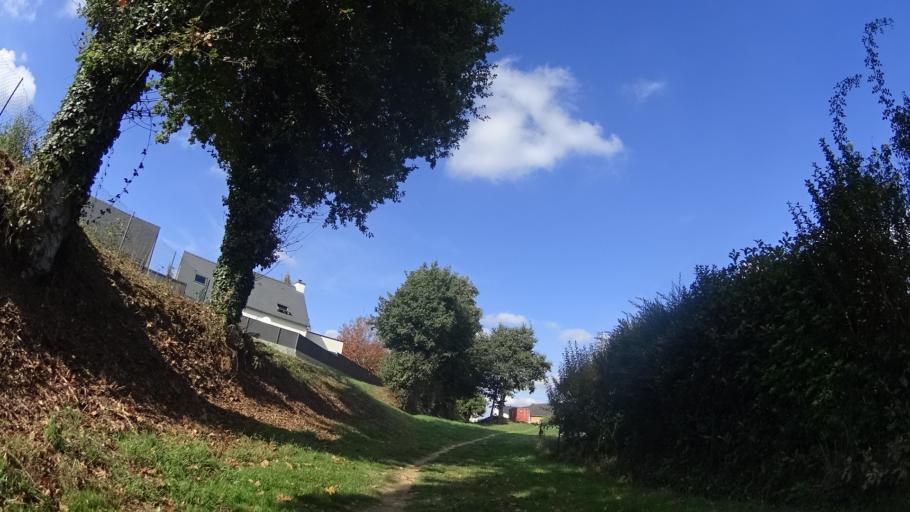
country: FR
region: Brittany
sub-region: Departement d'Ille-et-Vilaine
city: Geveze
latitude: 48.2247
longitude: -1.7918
